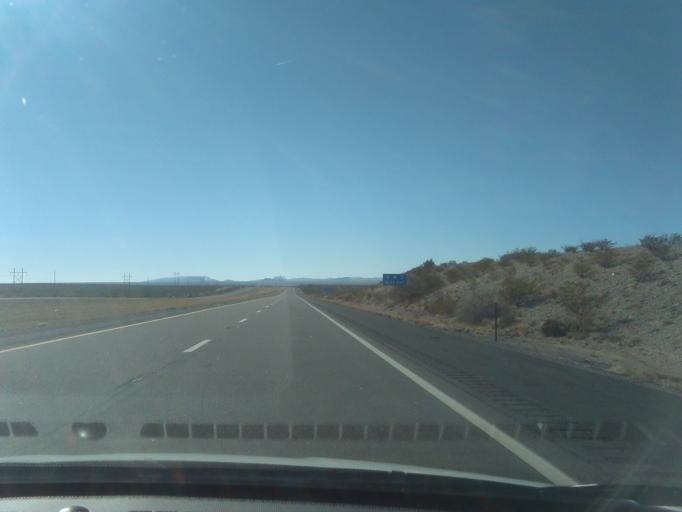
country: US
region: New Mexico
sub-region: Socorro County
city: Socorro
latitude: 33.6479
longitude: -107.1086
